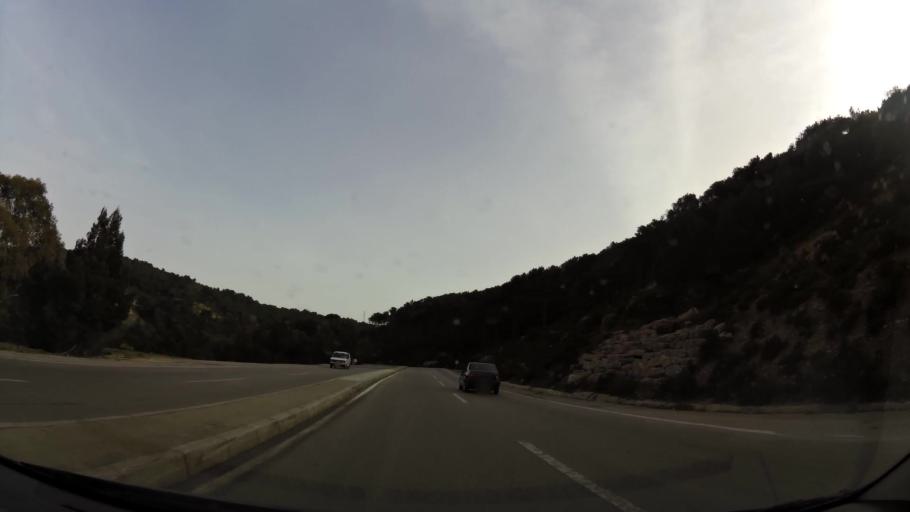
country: MA
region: Tanger-Tetouan
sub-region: Tanger-Assilah
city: Dar Chaoui
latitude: 35.5632
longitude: -5.5851
